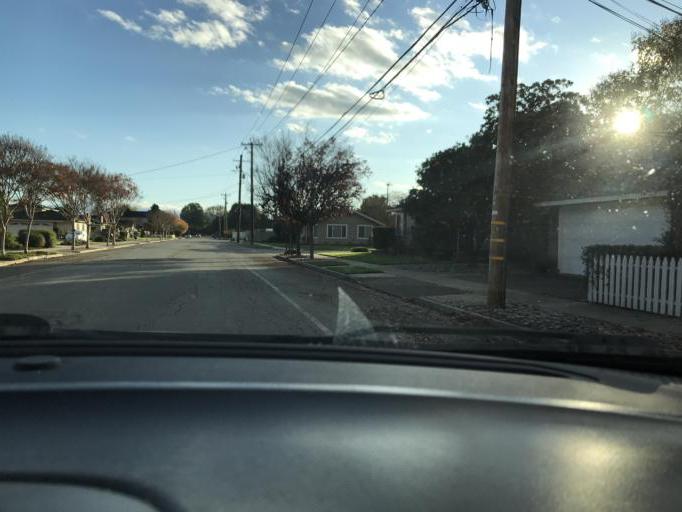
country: US
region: California
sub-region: Santa Clara County
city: Buena Vista
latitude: 37.2981
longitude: -121.9175
